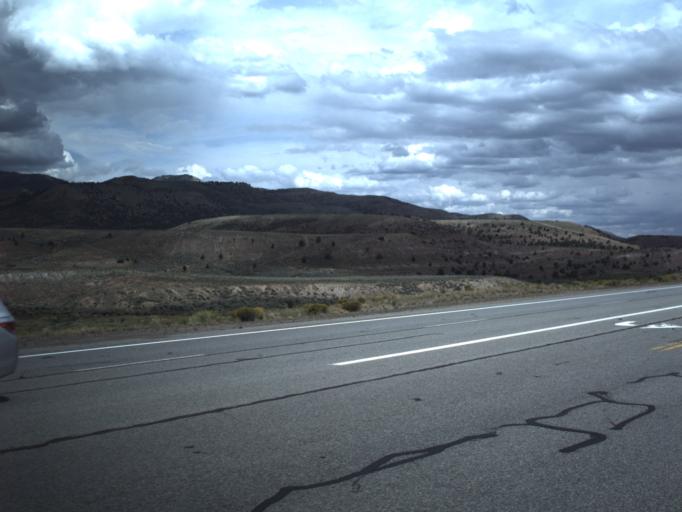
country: US
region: Utah
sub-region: Carbon County
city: Helper
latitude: 39.8394
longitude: -110.9853
